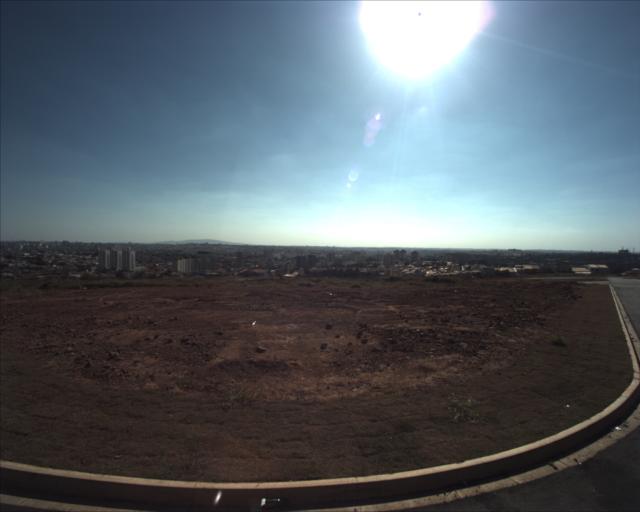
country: BR
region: Sao Paulo
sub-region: Sorocaba
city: Sorocaba
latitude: -23.5002
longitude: -47.4205
